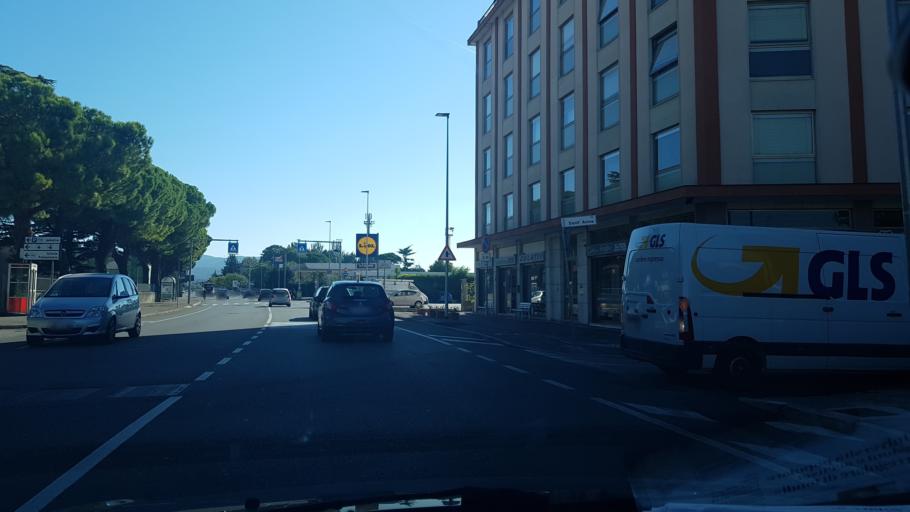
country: IT
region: Friuli Venezia Giulia
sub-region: Provincia di Gorizia
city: Monfalcone
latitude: 45.8026
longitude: 13.5400
